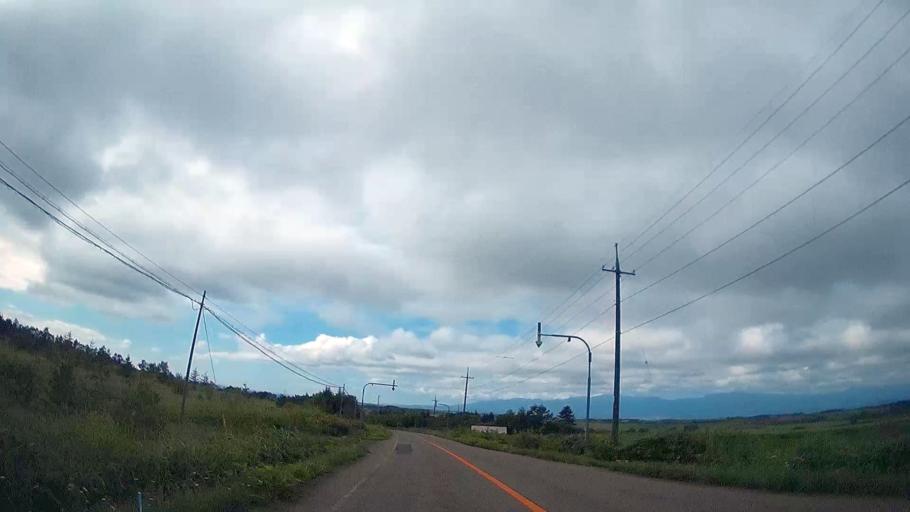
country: JP
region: Hokkaido
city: Nanae
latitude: 42.3110
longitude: 140.0067
